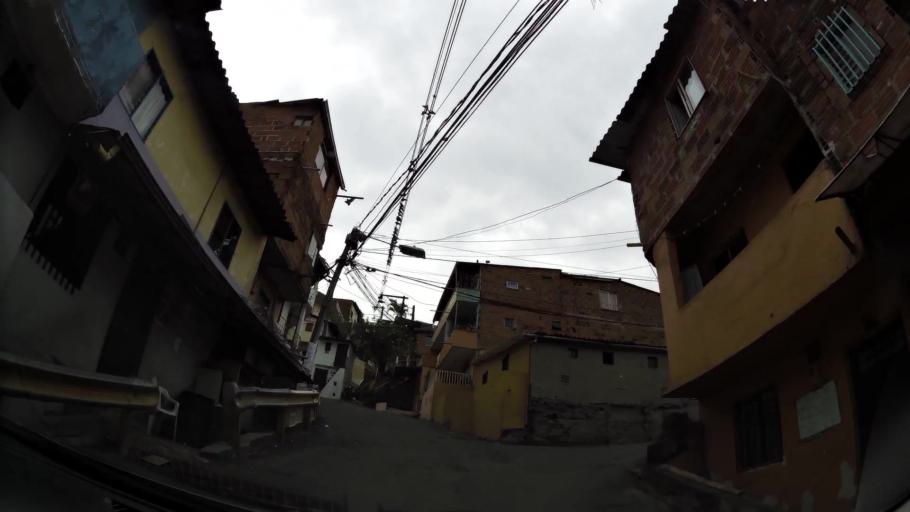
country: CO
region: Antioquia
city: Bello
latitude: 6.2953
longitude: -75.5521
